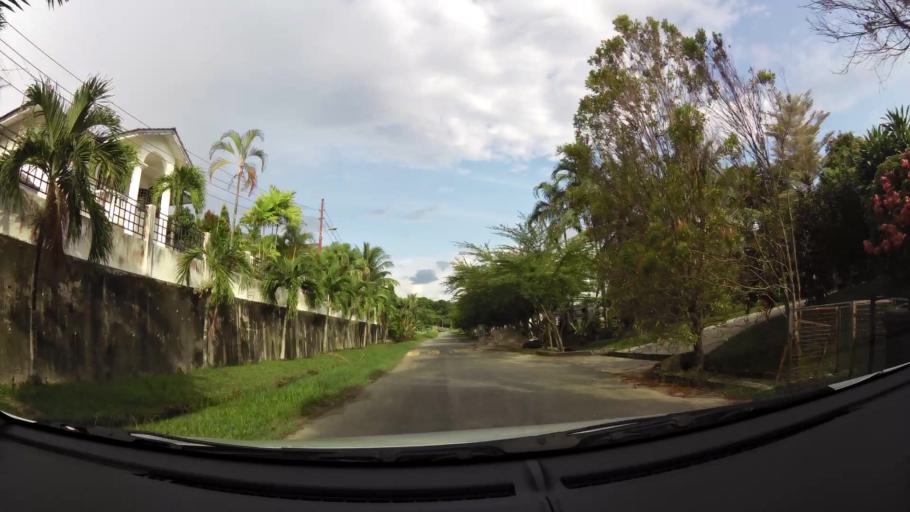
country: BN
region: Brunei and Muara
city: Bandar Seri Begawan
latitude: 4.9697
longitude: 114.9792
